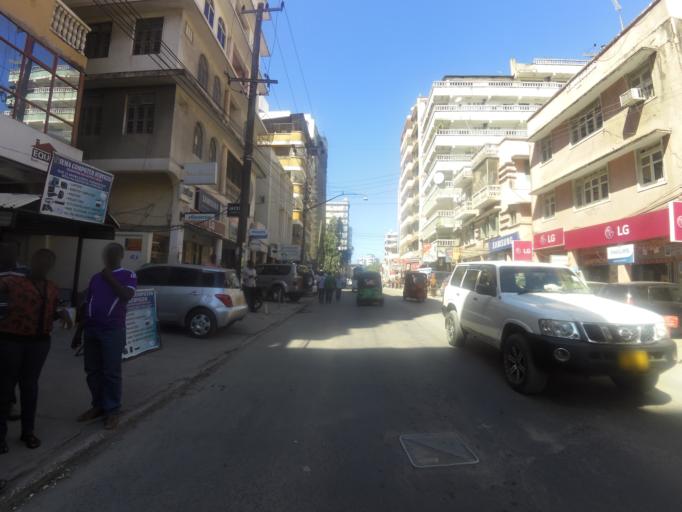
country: TZ
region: Dar es Salaam
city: Dar es Salaam
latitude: -6.8220
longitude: 39.2778
